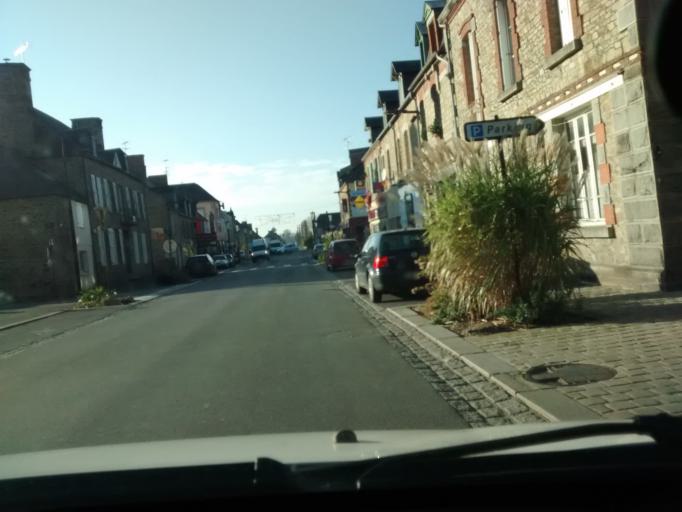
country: FR
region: Lower Normandy
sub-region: Departement de la Manche
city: Pontorson
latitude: 48.5528
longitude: -1.5116
